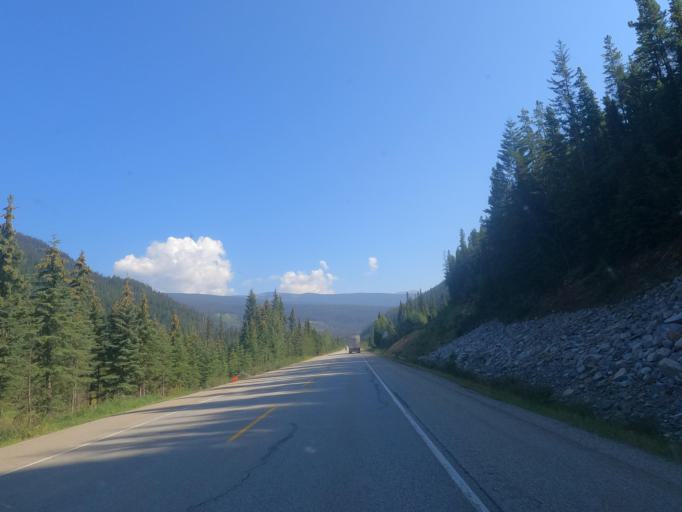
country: CA
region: Alberta
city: Jasper Park Lodge
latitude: 52.8769
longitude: -118.4953
